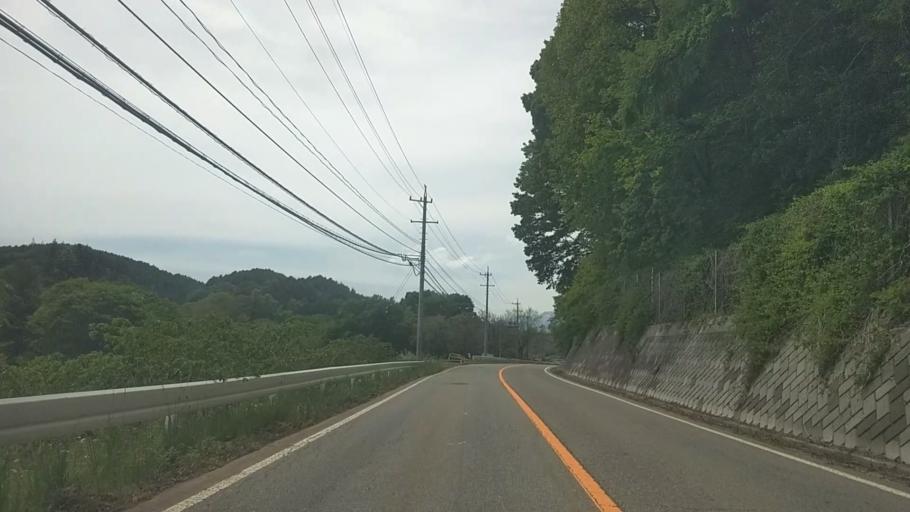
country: JP
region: Nagano
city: Saku
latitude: 36.1260
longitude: 138.4560
